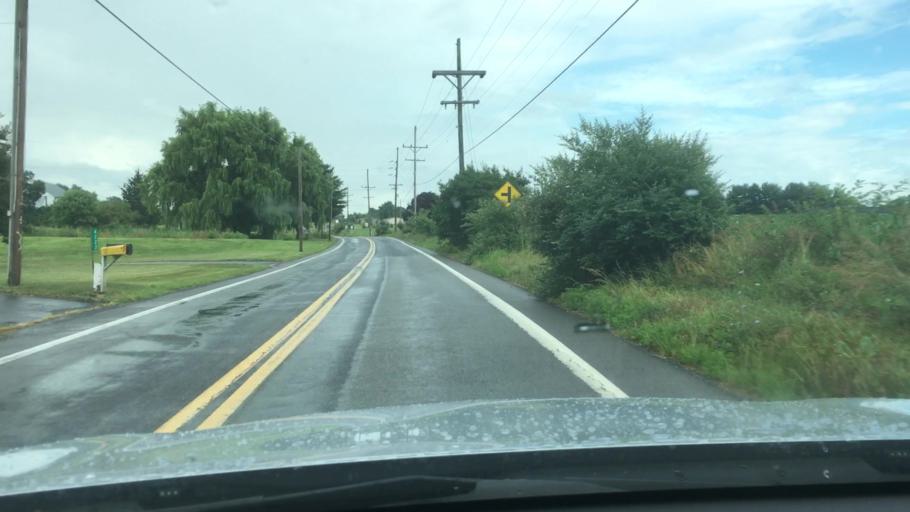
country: US
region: Pennsylvania
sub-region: Franklin County
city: Greencastle
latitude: 39.8664
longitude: -77.7758
